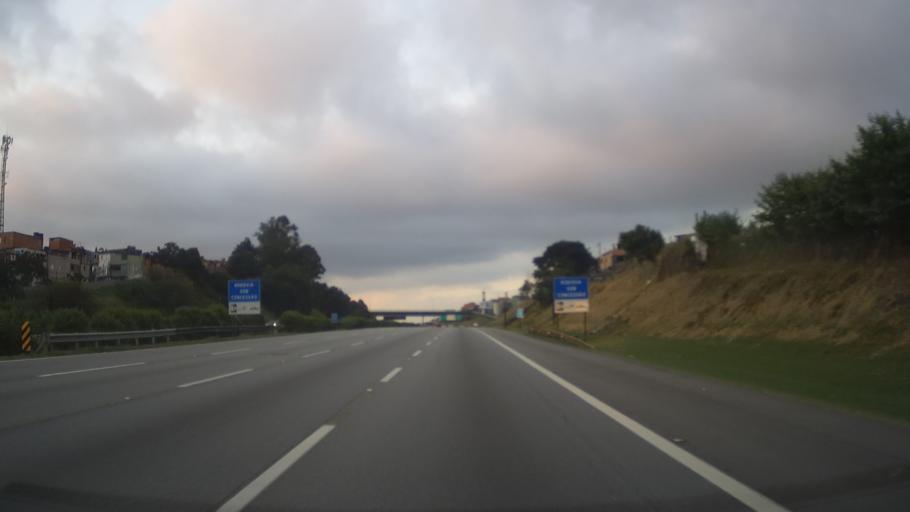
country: BR
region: Sao Paulo
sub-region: Diadema
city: Diadema
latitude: -23.7087
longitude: -46.6033
